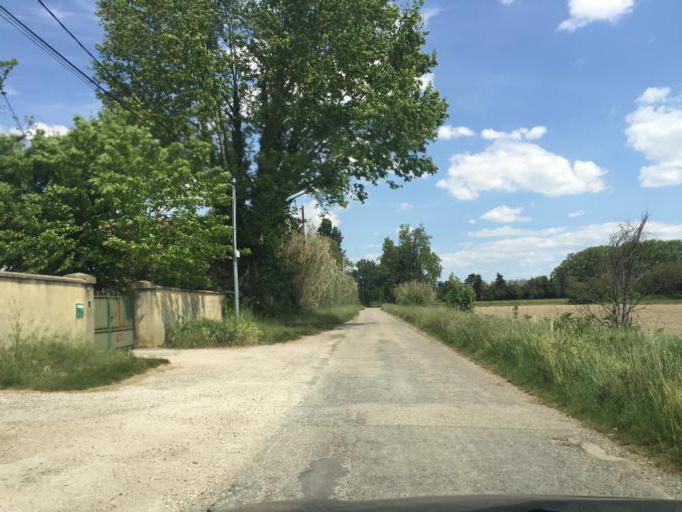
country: FR
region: Provence-Alpes-Cote d'Azur
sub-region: Departement du Vaucluse
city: Jonquieres
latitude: 44.1297
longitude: 4.9086
